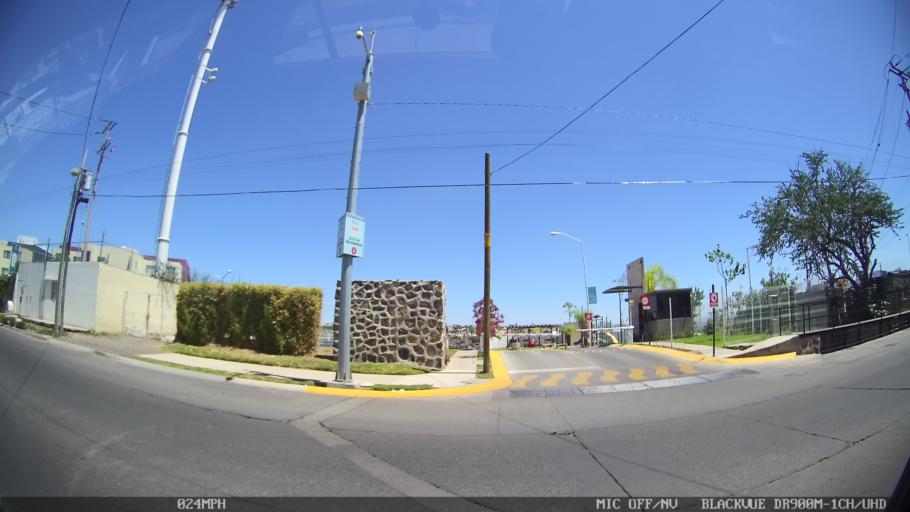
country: MX
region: Jalisco
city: Tlaquepaque
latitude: 20.6838
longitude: -103.2868
